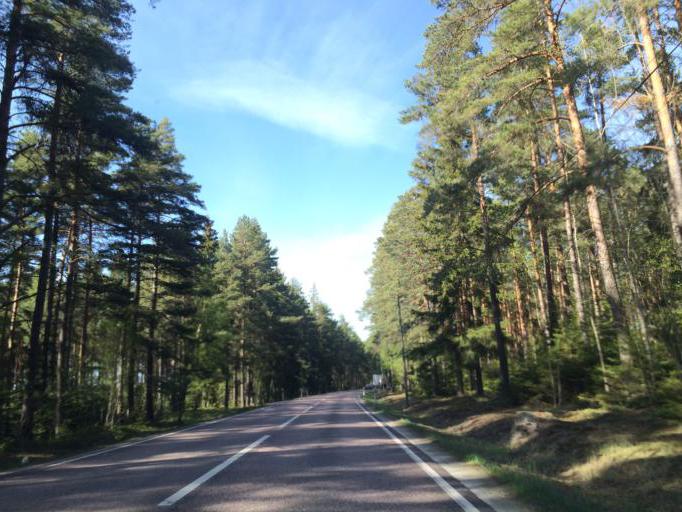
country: SE
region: Vaestmanland
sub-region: Kungsors Kommun
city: Kungsoer
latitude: 59.3010
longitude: 16.1067
